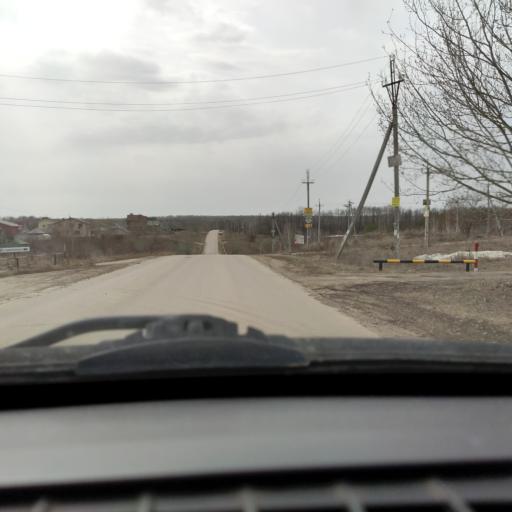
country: RU
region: Samara
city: Dubovyy Umet
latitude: 53.0431
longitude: 50.1793
